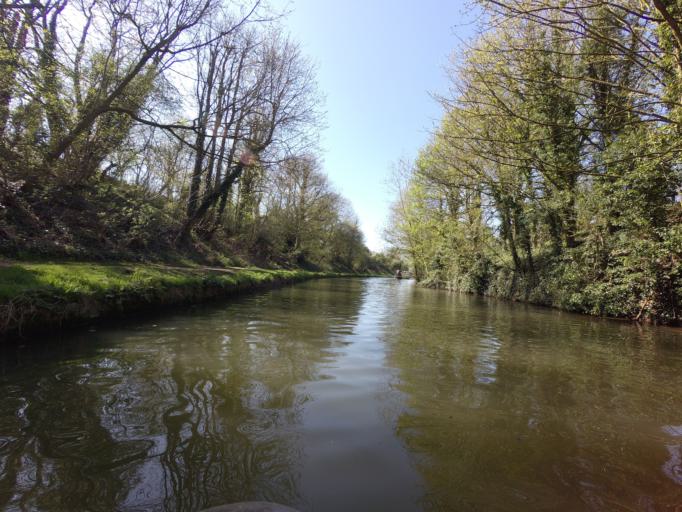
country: GB
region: England
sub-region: Hertfordshire
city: Tring
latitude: 51.8117
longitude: -0.6445
